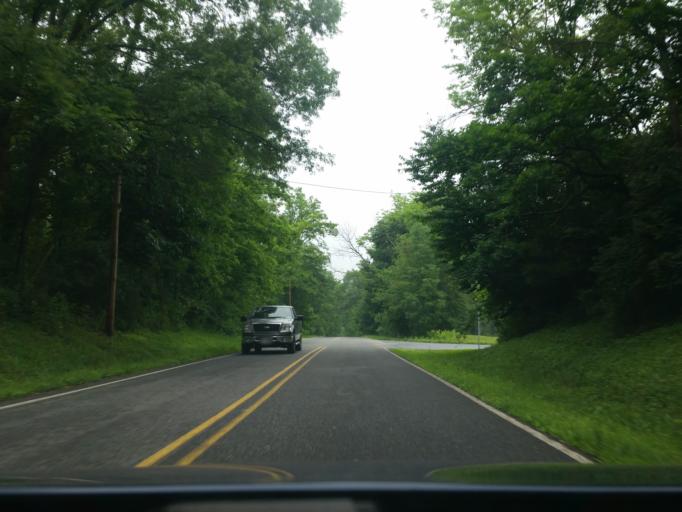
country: US
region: Pennsylvania
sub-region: Lebanon County
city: Jonestown
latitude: 40.4223
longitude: -76.5421
